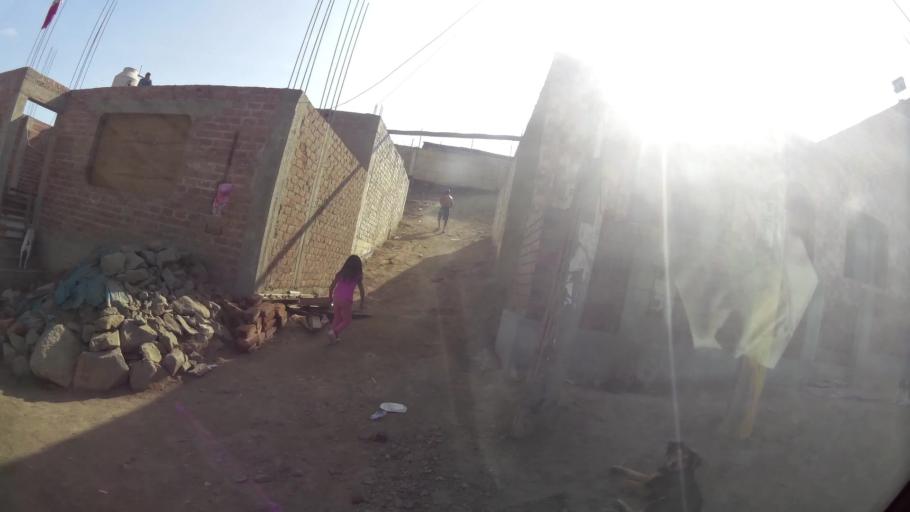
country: PE
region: Lima
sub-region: Huaura
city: Huacho
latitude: -11.1263
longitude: -77.6175
